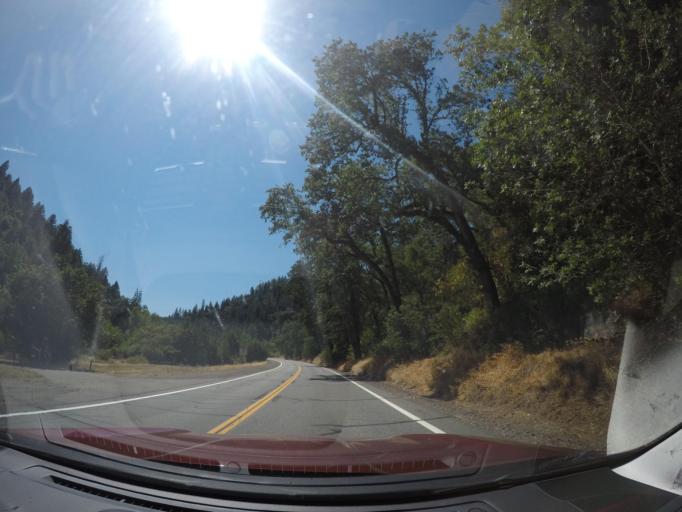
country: US
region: California
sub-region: Shasta County
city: Bella Vista
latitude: 40.7515
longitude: -122.0424
